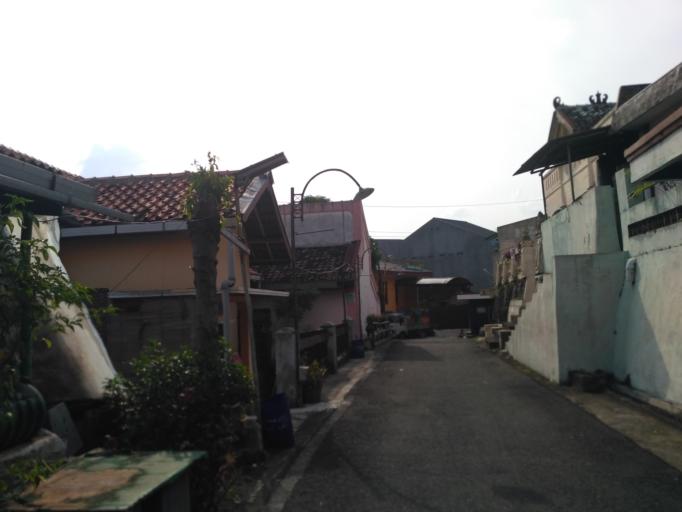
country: ID
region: Central Java
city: Semarang
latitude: -7.0150
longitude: 110.4497
